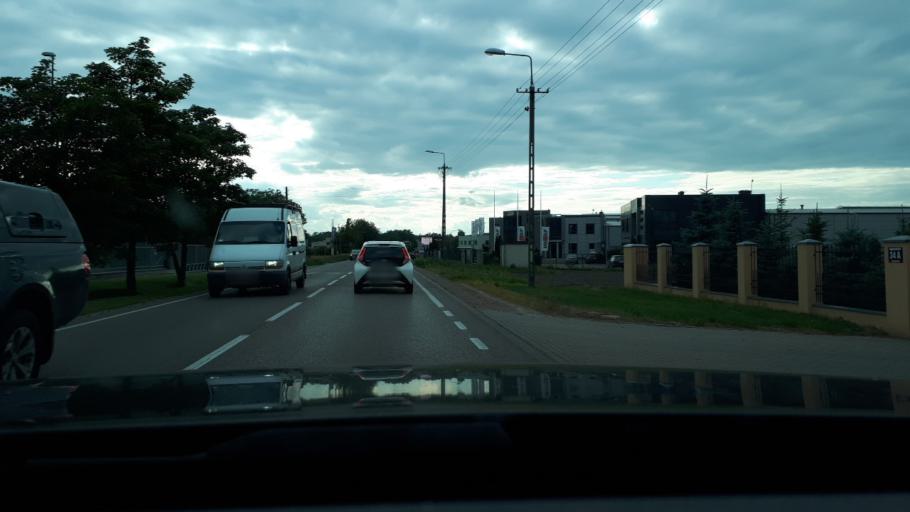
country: PL
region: Masovian Voivodeship
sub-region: Powiat pruszkowski
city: Michalowice
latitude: 52.1442
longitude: 20.8619
